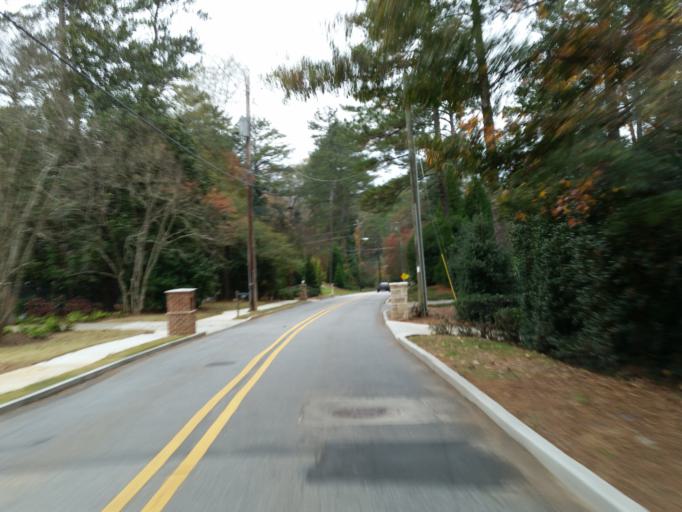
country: US
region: Georgia
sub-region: Fulton County
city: Sandy Springs
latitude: 33.8929
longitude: -84.4048
